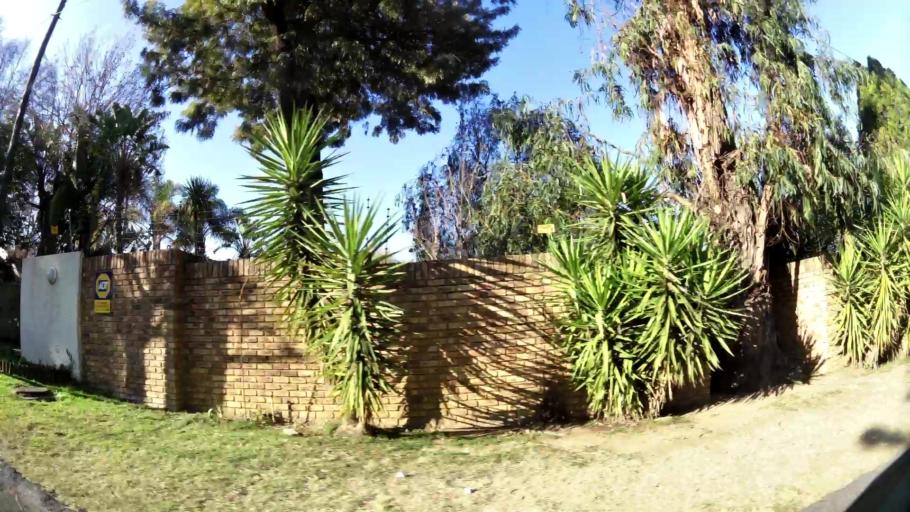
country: ZA
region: Gauteng
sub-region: City of Johannesburg Metropolitan Municipality
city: Johannesburg
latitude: -26.1156
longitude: 28.0658
